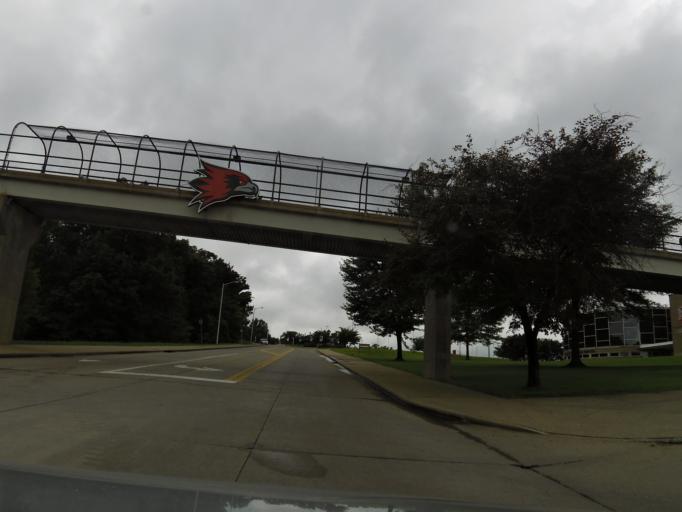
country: US
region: Missouri
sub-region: Cape Girardeau County
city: Cape Girardeau
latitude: 37.3190
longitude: -89.5274
